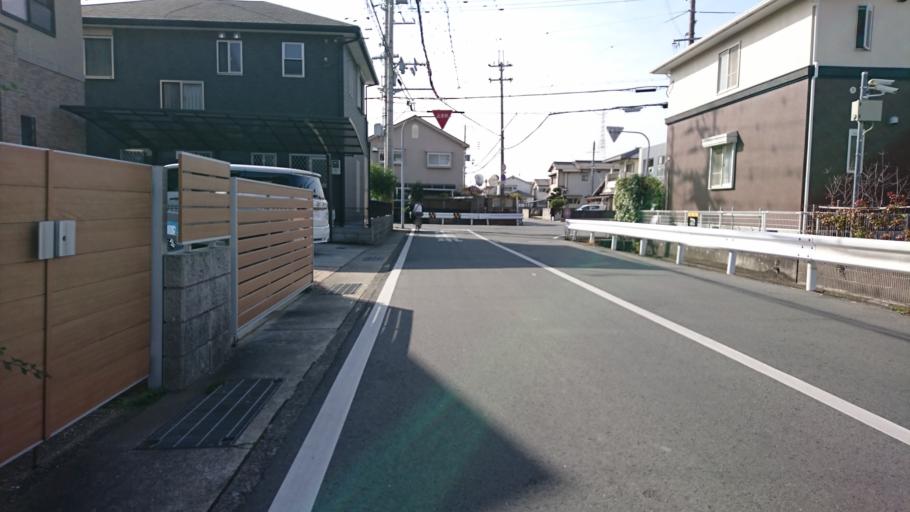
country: JP
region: Hyogo
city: Kakogawacho-honmachi
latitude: 34.7425
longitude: 134.8403
